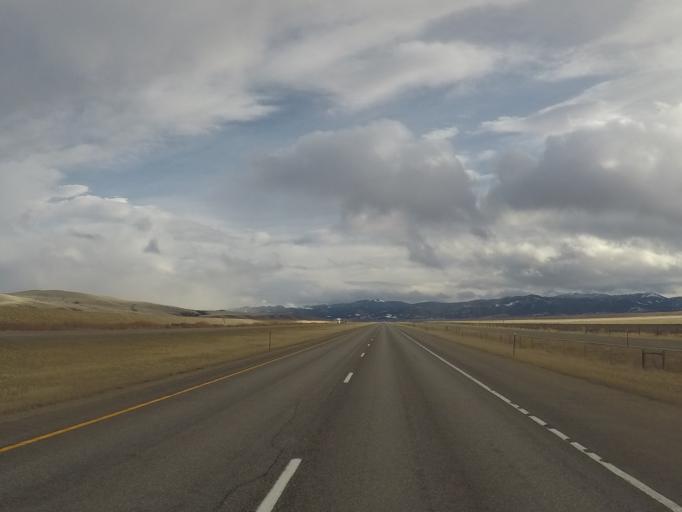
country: US
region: Montana
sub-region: Deer Lodge County
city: Warm Springs
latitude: 46.1627
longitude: -112.7912
